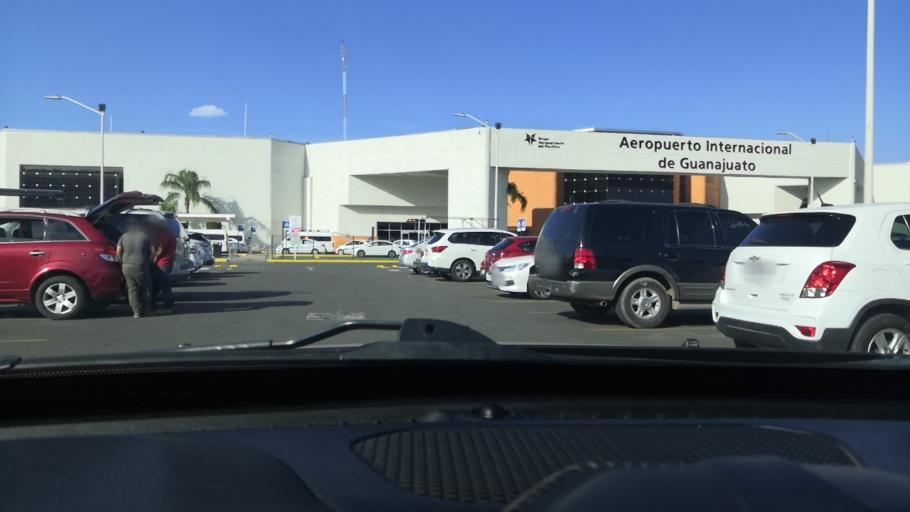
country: MX
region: Guanajuato
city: Colonia Nuevo Mexico
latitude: 20.9854
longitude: -101.4799
